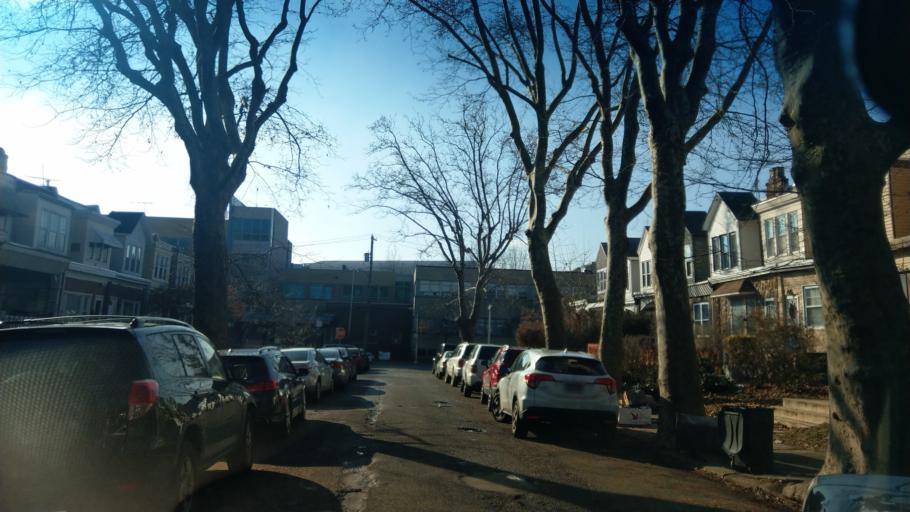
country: US
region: Pennsylvania
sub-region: Montgomery County
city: Rockledge
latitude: 40.0202
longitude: -75.1218
